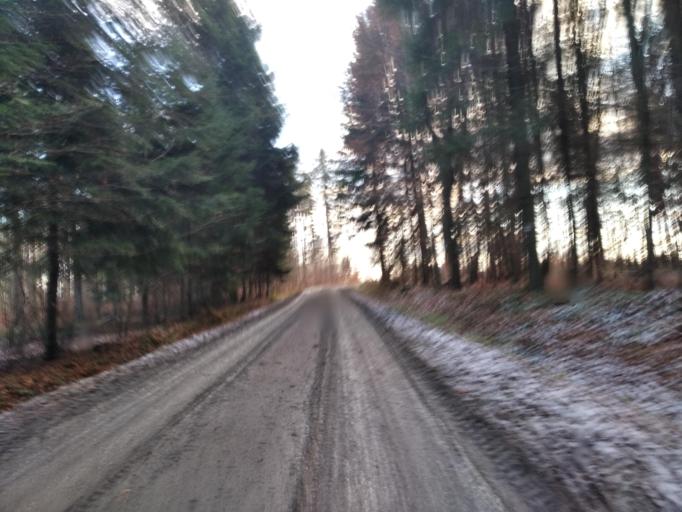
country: PL
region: Subcarpathian Voivodeship
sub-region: Powiat strzyzowski
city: Babica
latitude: 49.9519
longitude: 21.8697
